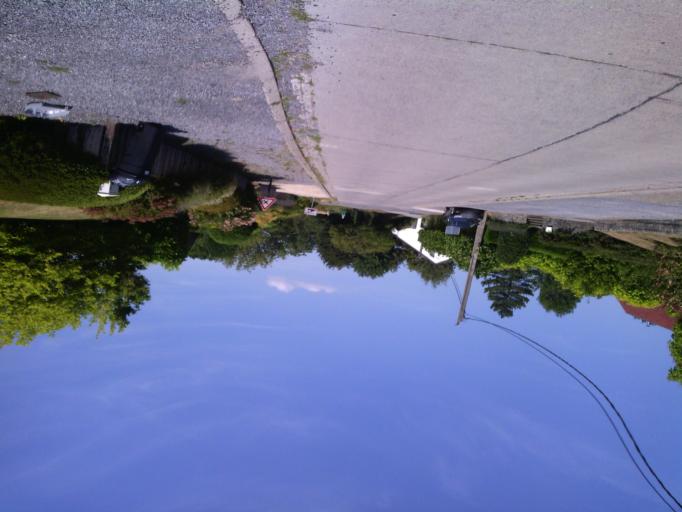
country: BE
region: Wallonia
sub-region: Province du Hainaut
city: Antoing
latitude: 50.6211
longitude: 3.4489
